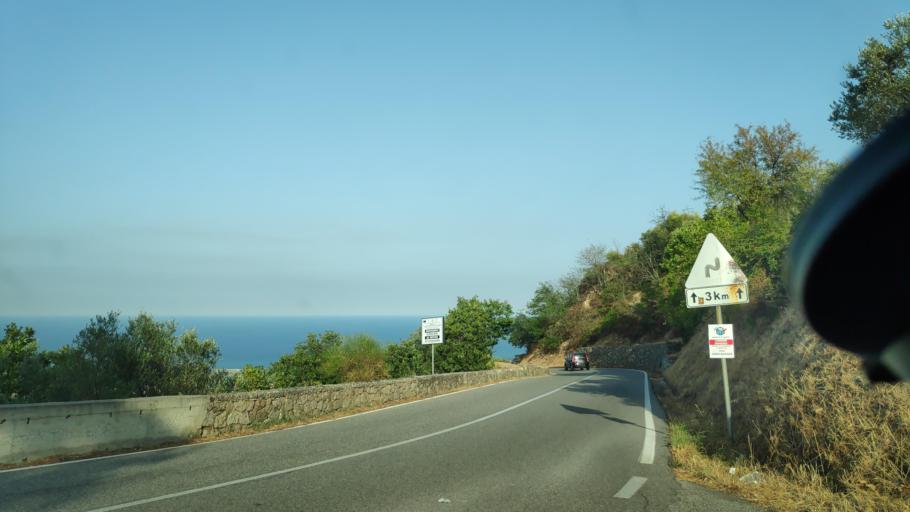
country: IT
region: Calabria
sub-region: Provincia di Catanzaro
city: Sant'Andrea Apostolo dello Ionio
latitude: 38.6174
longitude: 16.5335
